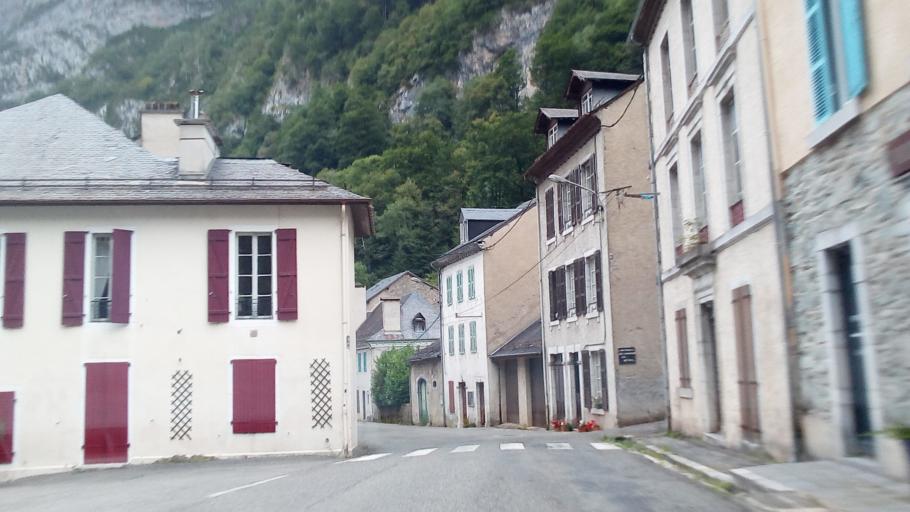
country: FR
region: Aquitaine
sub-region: Departement des Pyrenees-Atlantiques
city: Laruns
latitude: 42.9523
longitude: -0.4401
